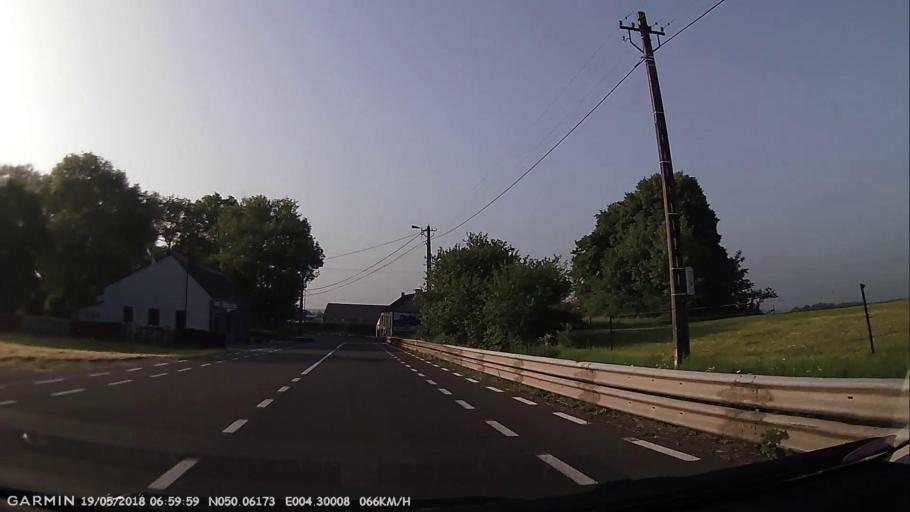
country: BE
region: Wallonia
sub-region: Province du Hainaut
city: Chimay
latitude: 50.0615
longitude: 4.3003
